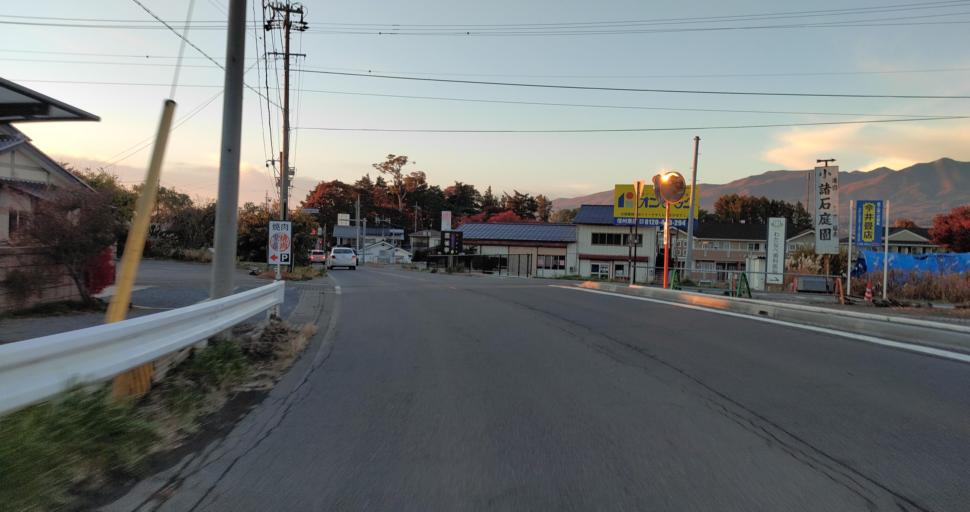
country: JP
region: Nagano
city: Komoro
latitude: 36.2928
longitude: 138.4593
